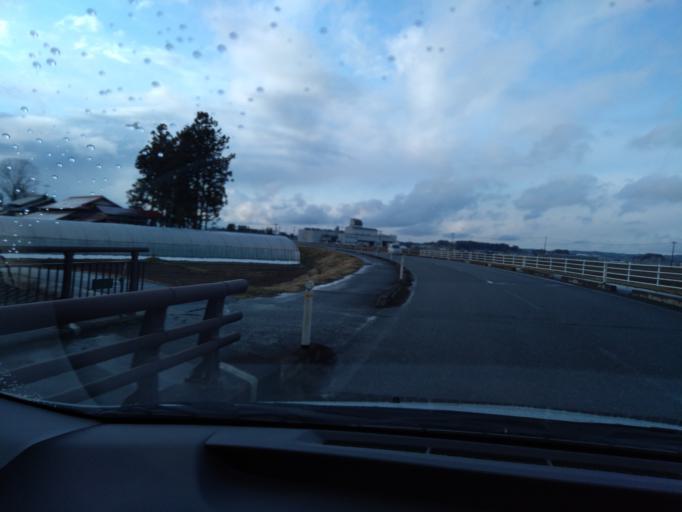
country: JP
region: Iwate
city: Ichinoseki
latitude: 38.7561
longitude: 141.1176
